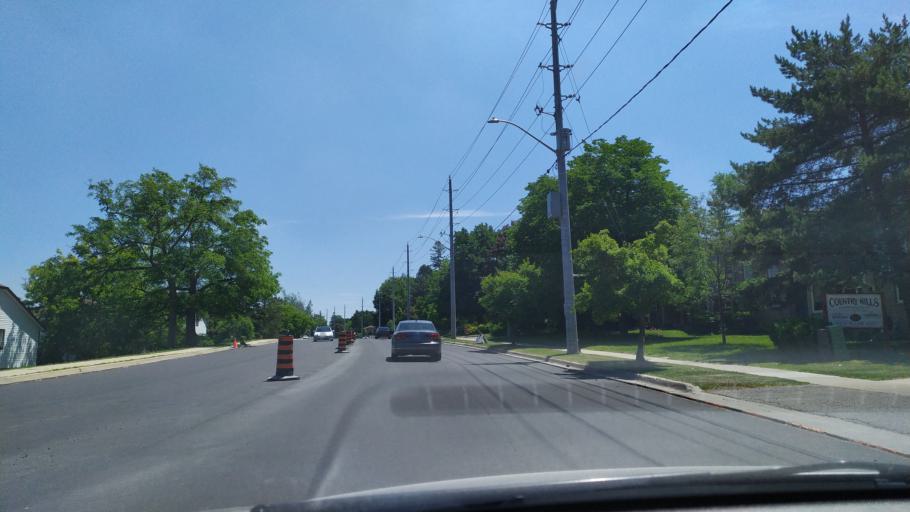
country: CA
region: Ontario
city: Kitchener
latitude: 43.3947
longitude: -80.4454
